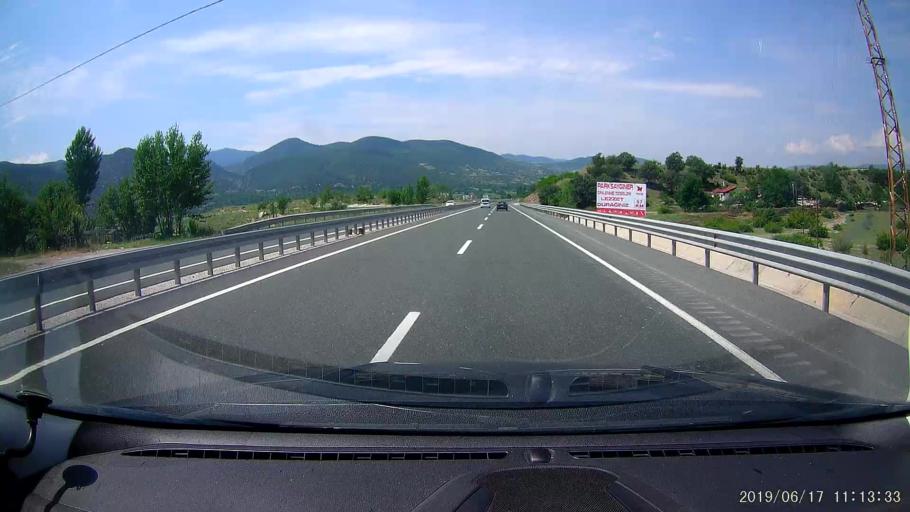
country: TR
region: Kastamonu
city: Tosya
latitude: 40.9605
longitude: 33.9700
